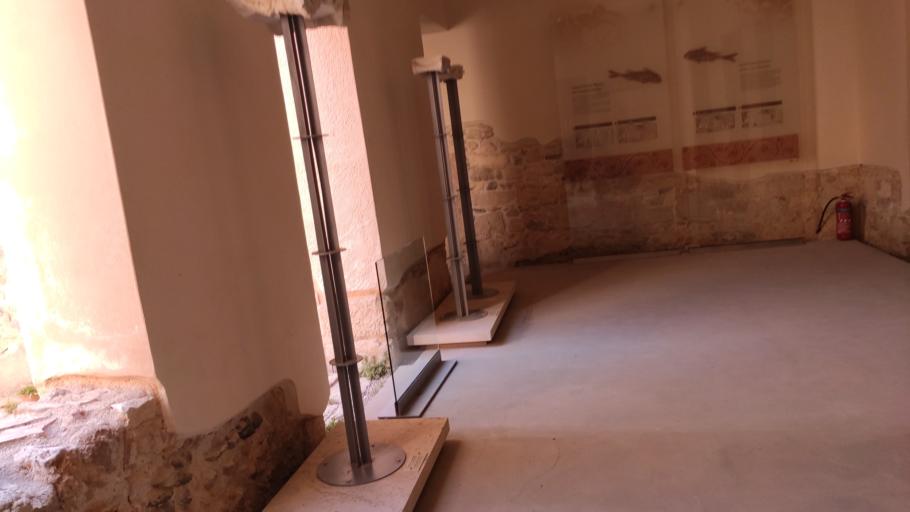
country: GR
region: South Aegean
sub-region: Nomos Dodekanisou
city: Kos
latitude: 36.8900
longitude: 27.2886
